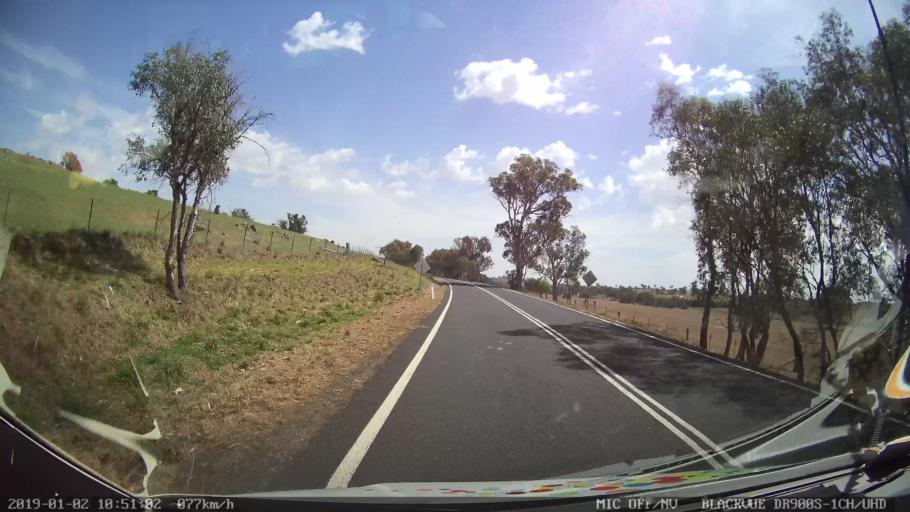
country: AU
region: New South Wales
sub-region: Cootamundra
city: Cootamundra
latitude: -34.7054
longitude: 148.2756
